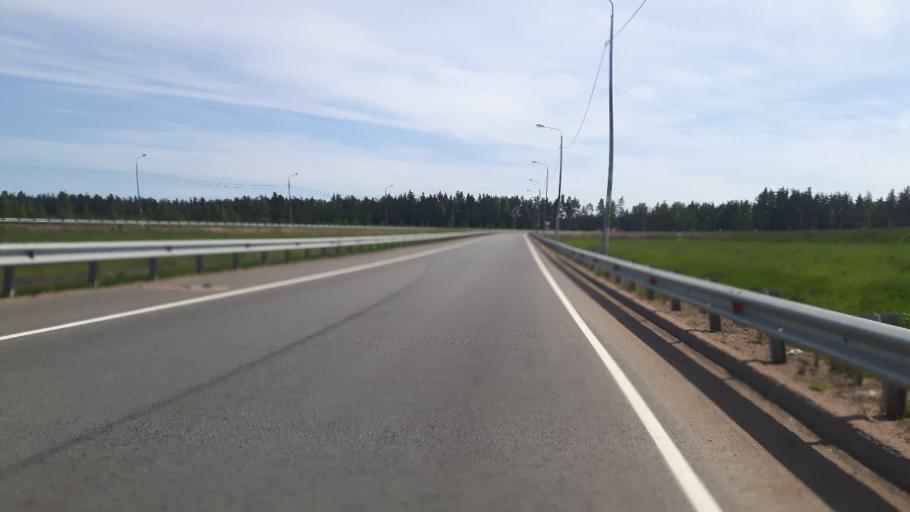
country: RU
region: Leningrad
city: Vistino
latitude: 59.6635
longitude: 28.4356
